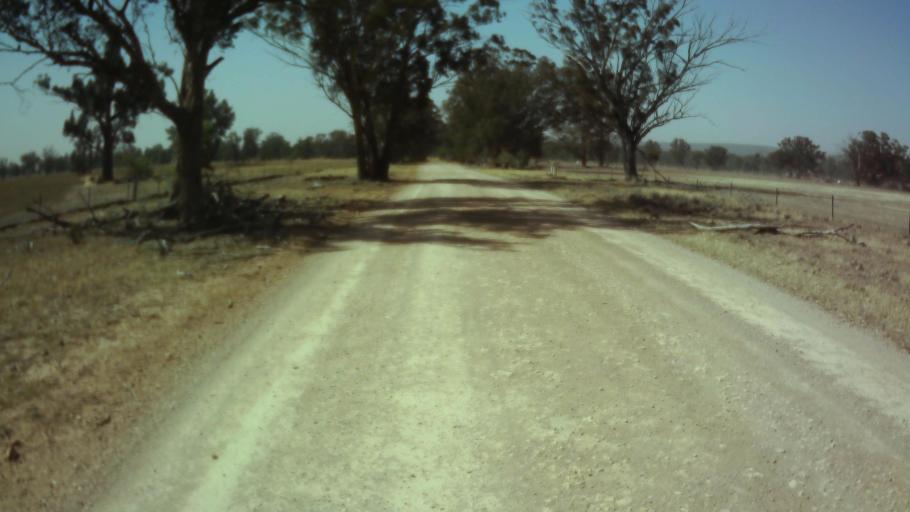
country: AU
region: New South Wales
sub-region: Weddin
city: Grenfell
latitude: -34.0029
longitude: 147.9178
